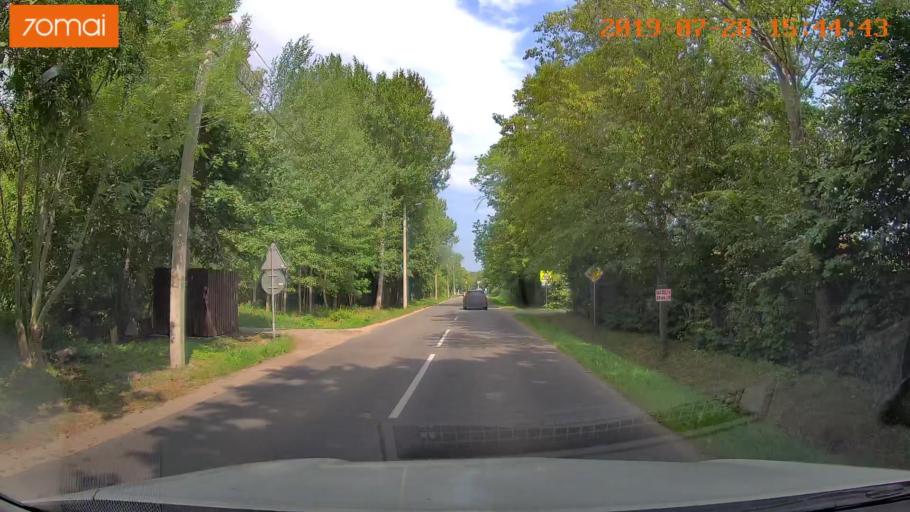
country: RU
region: Kaliningrad
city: Donskoye
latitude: 54.9405
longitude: 20.0331
